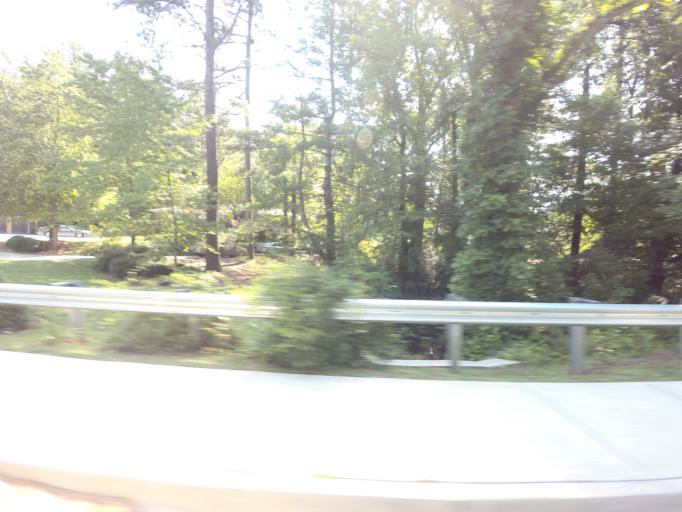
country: US
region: Georgia
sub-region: Fulton County
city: Alpharetta
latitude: 34.0274
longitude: -84.2693
